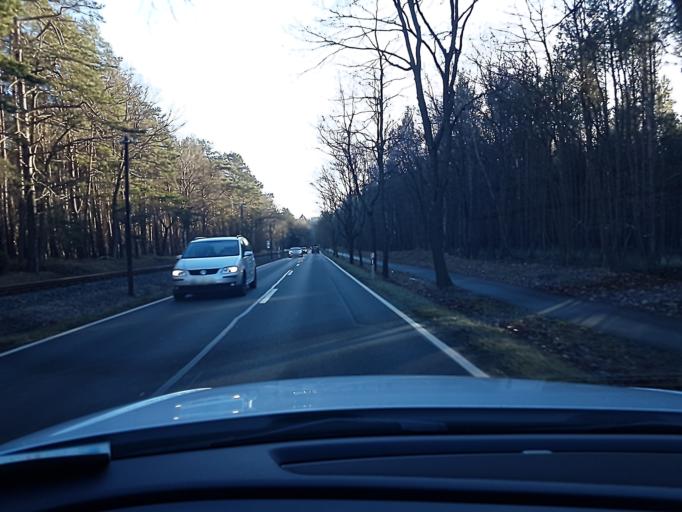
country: DE
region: Mecklenburg-Vorpommern
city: Ostseebad Sellin
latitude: 54.3500
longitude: 13.7051
